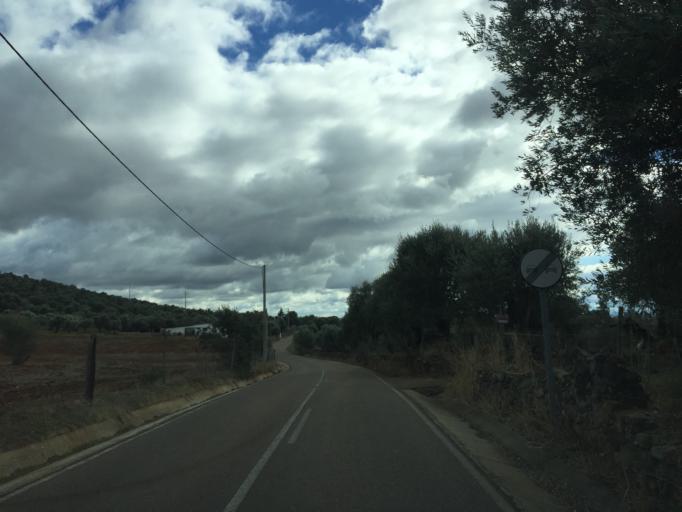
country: PT
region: Portalegre
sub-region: Alter do Chao
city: Alter do Chao
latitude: 39.2115
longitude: -7.6671
